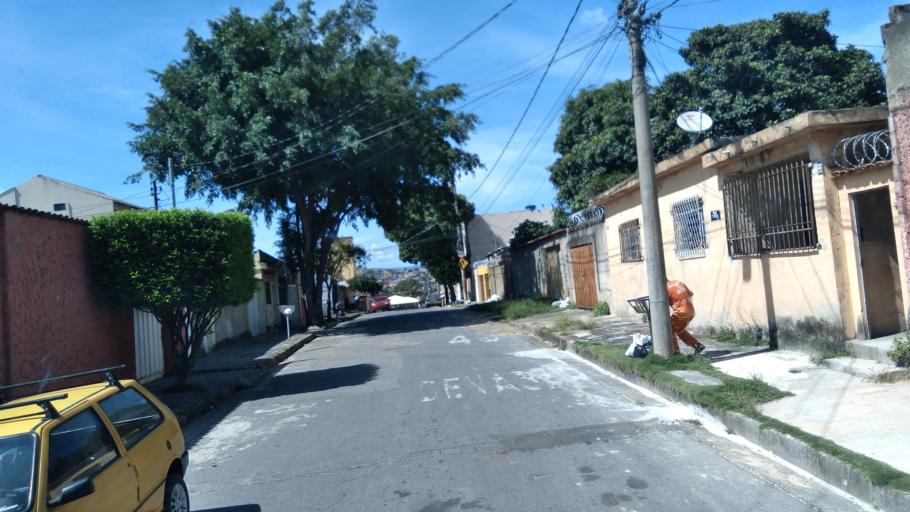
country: BR
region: Minas Gerais
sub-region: Contagem
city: Contagem
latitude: -19.8914
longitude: -44.0143
